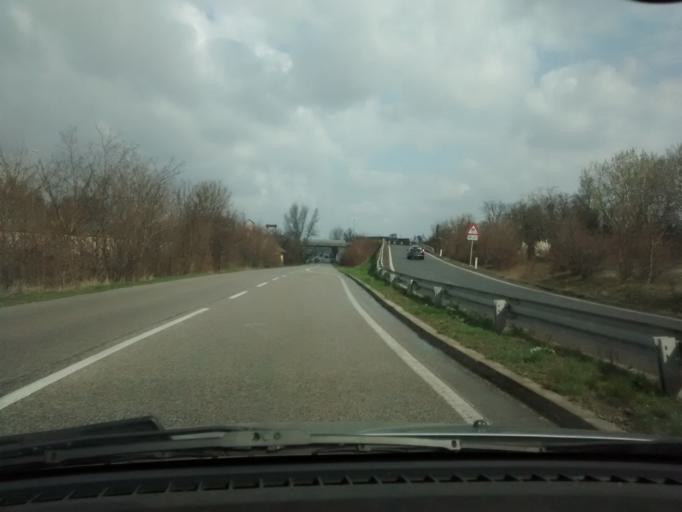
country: AT
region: Lower Austria
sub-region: Politischer Bezirk Modling
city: Wiener Neudorf
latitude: 48.0976
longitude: 16.3150
